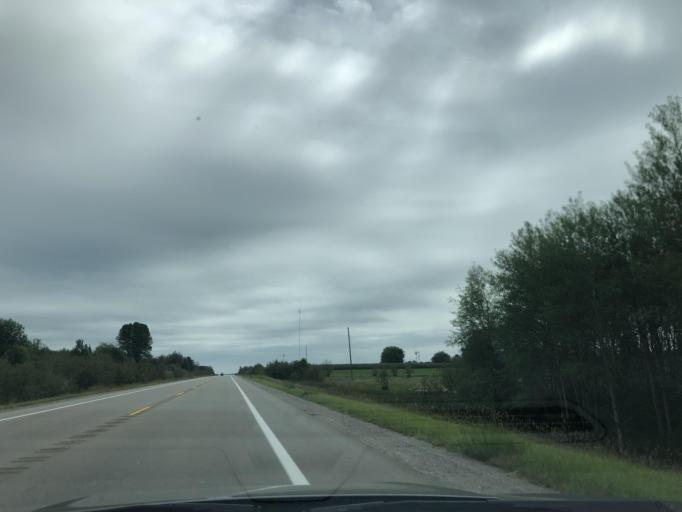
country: US
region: Michigan
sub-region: Clare County
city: Harrison
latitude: 44.0312
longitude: -84.9658
